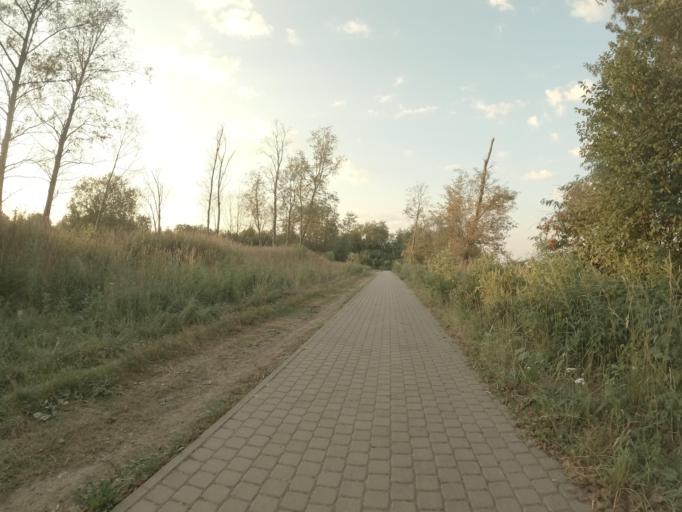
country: RU
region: Leningrad
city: Kirovsk
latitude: 59.8537
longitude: 30.9502
